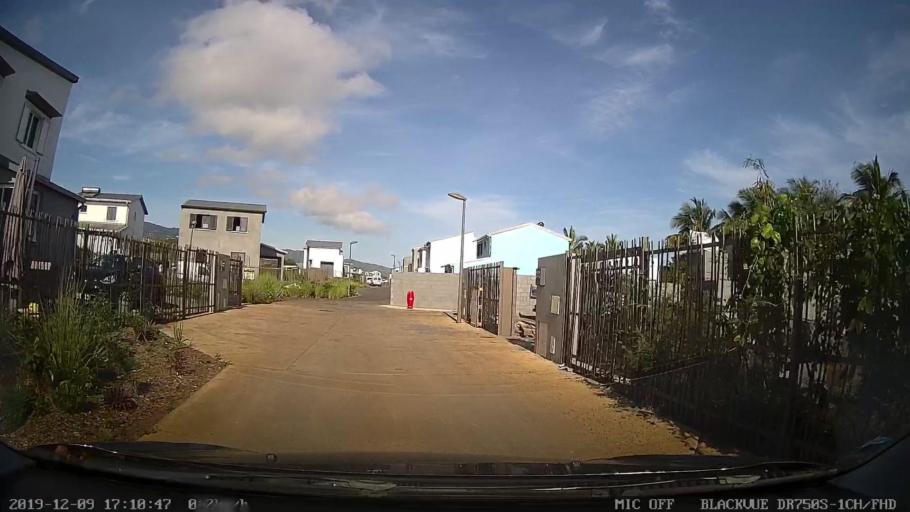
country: RE
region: Reunion
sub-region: Reunion
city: Sainte-Marie
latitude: -20.9077
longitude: 55.5190
